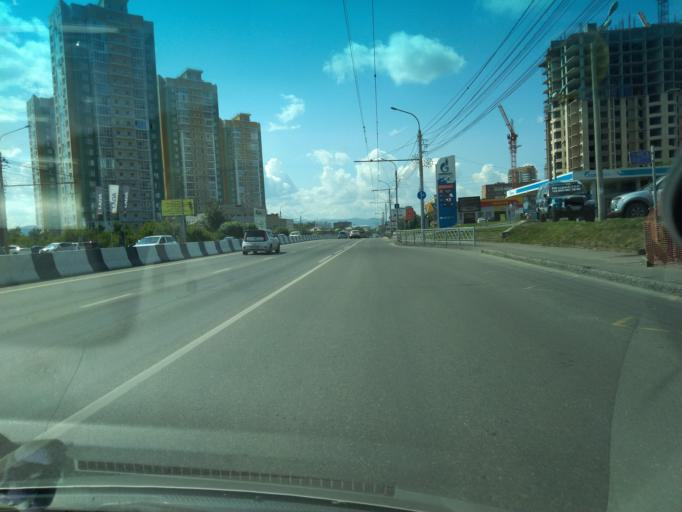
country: RU
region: Krasnoyarskiy
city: Krasnoyarsk
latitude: 56.0349
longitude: 92.9260
